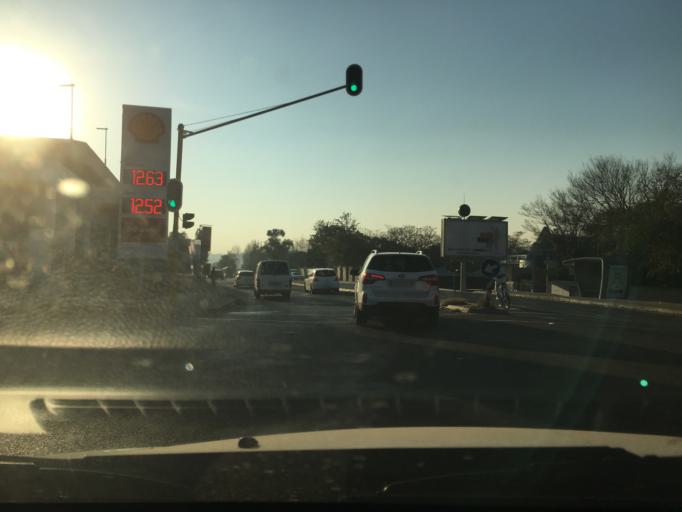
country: ZA
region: Gauteng
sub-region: City of Johannesburg Metropolitan Municipality
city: Johannesburg
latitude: -26.0758
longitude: 28.0271
